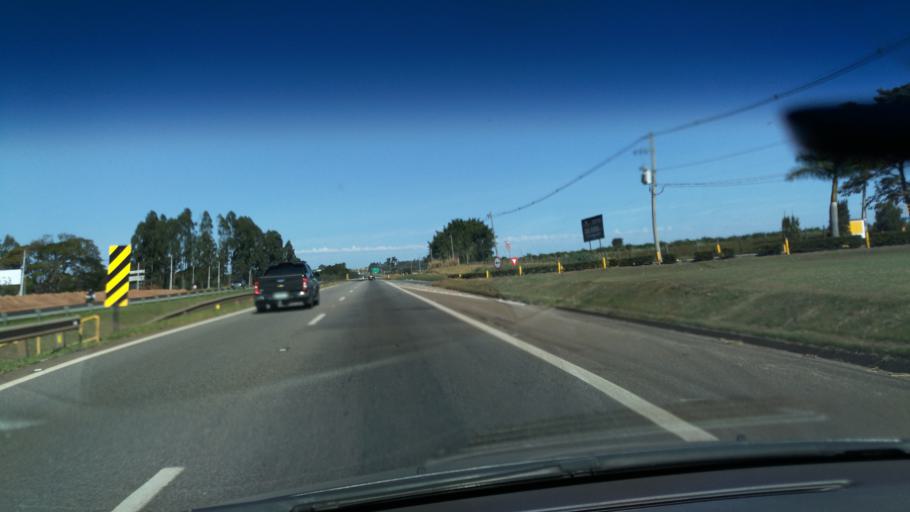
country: BR
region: Sao Paulo
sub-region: Santo Antonio De Posse
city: Santo Antonio de Posse
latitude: -22.6100
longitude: -47.0075
